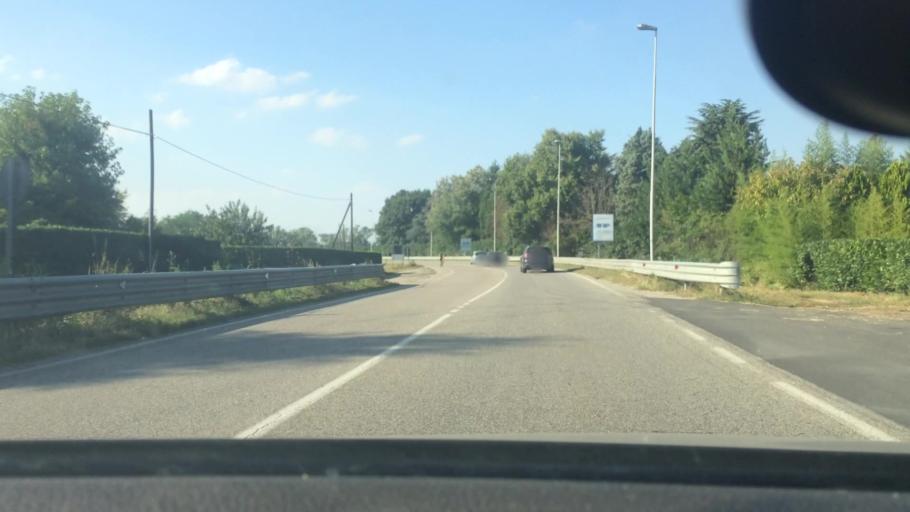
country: IT
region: Lombardy
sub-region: Citta metropolitana di Milano
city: Inveruno
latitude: 45.5215
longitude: 8.8564
